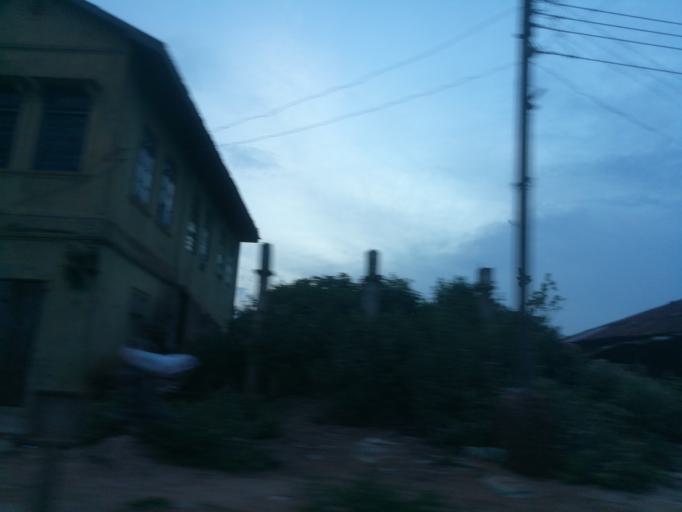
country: NG
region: Oyo
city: Ibadan
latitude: 7.3733
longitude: 3.9025
